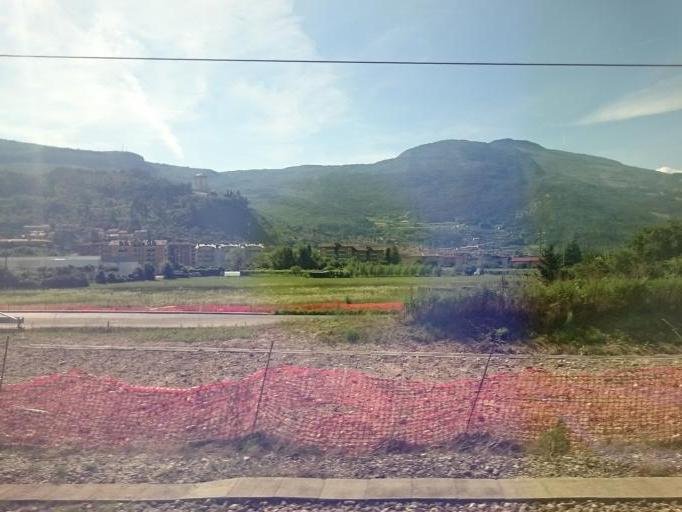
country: IT
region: Trentino-Alto Adige
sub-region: Provincia di Trento
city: Rovereto
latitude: 45.8761
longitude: 11.0246
